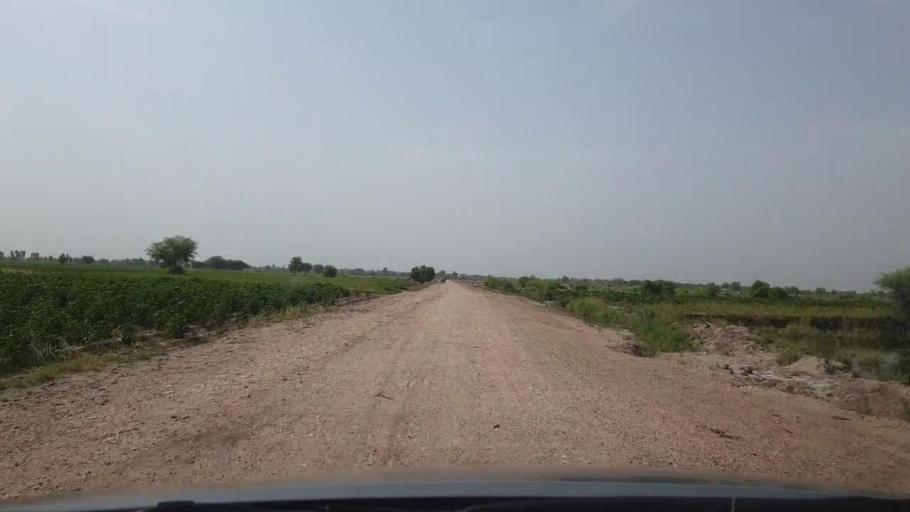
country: PK
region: Sindh
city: Rohri
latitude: 27.6721
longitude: 69.0130
